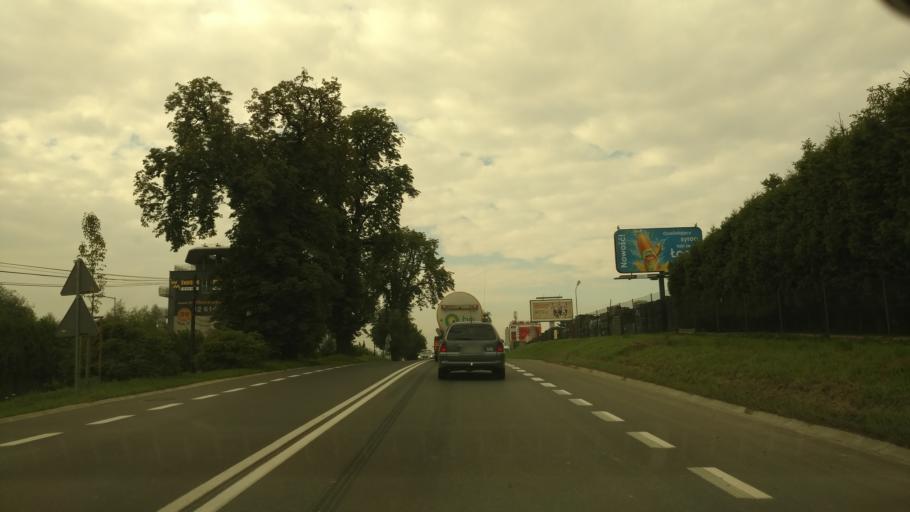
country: PL
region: Lesser Poland Voivodeship
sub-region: Powiat krakowski
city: Zielonki
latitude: 50.1011
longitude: 19.9632
